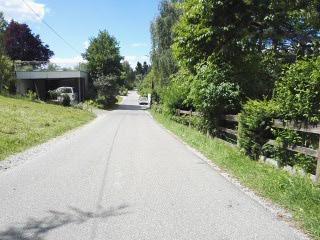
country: AT
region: Styria
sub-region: Graz Stadt
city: Mariatrost
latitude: 47.0819
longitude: 15.5352
